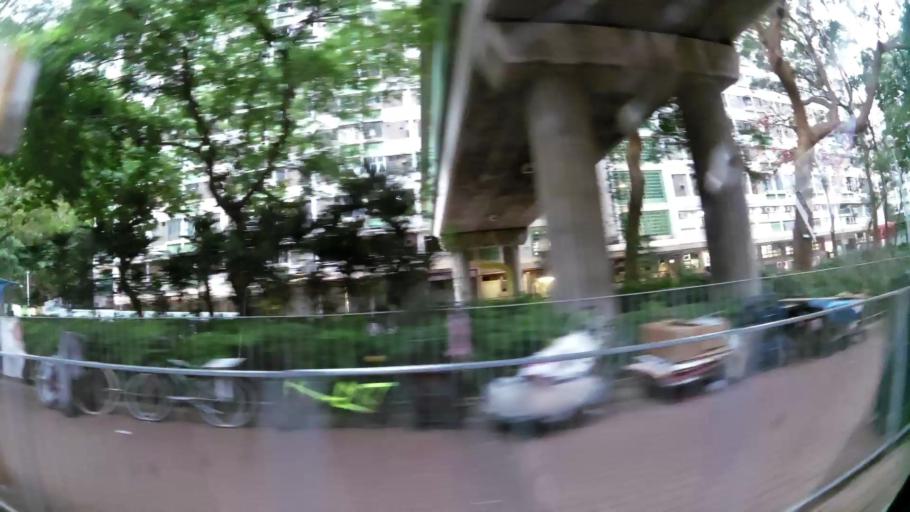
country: HK
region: Tsuen Wan
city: Tsuen Wan
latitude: 22.3679
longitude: 114.1231
